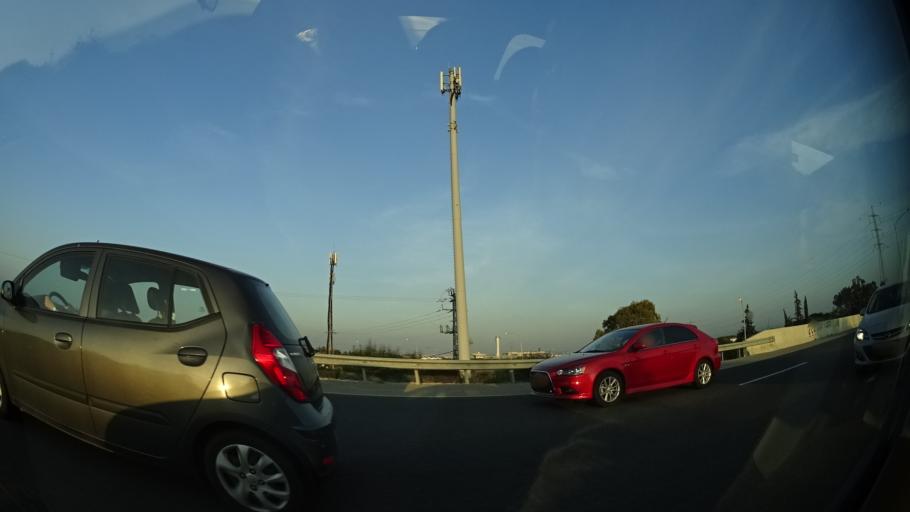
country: IL
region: Central District
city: Kefar Habad
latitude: 31.9957
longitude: 34.8541
